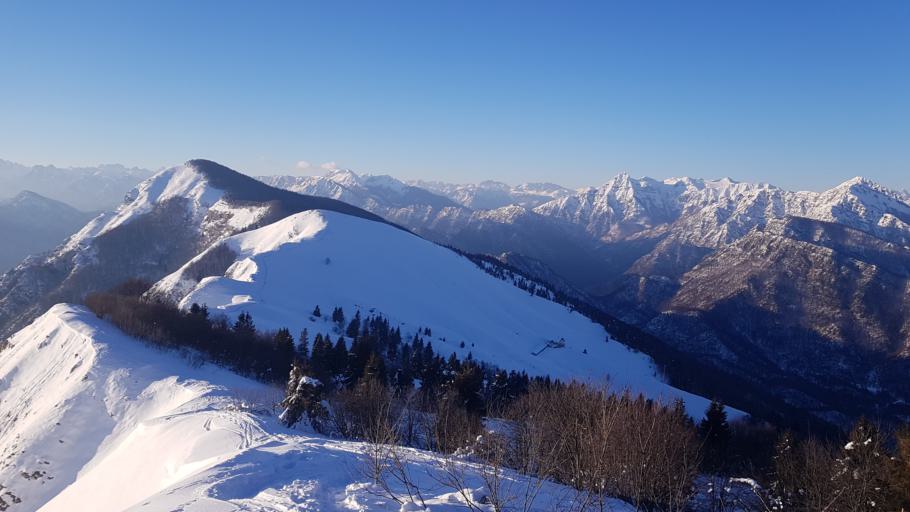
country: IT
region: Friuli Venezia Giulia
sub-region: Provincia di Pordenone
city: Anduins
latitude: 46.2767
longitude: 12.9922
